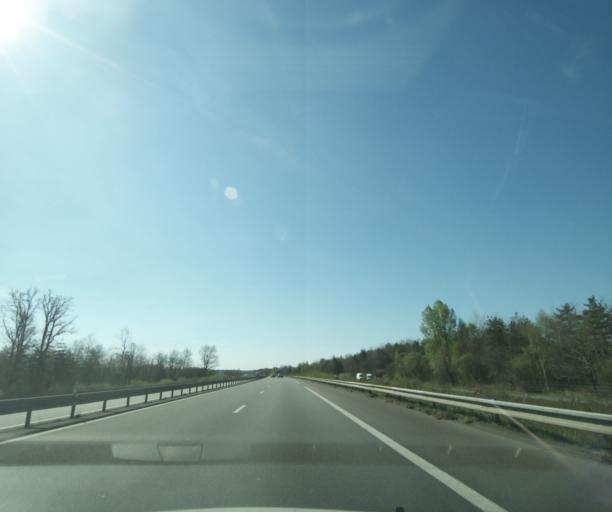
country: FR
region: Centre
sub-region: Departement du Loir-et-Cher
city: Theillay
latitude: 47.3376
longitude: 2.0475
